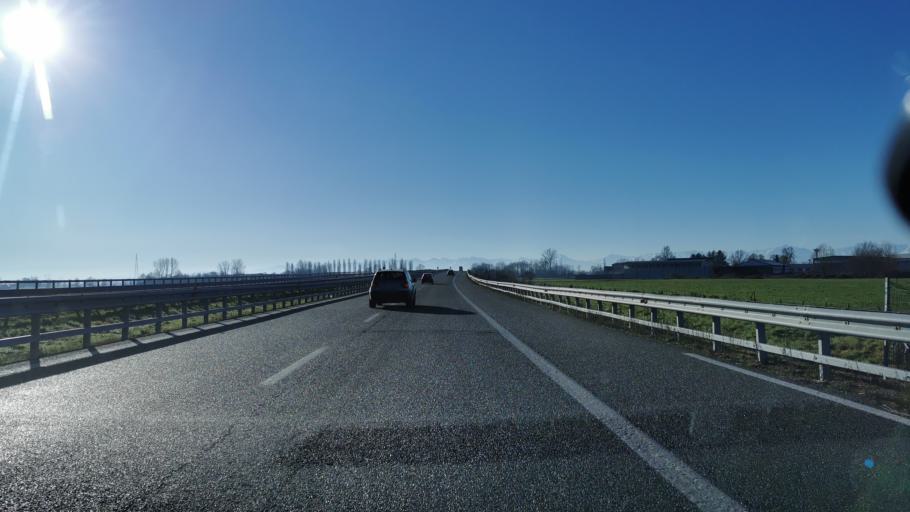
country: IT
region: Piedmont
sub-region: Provincia di Cuneo
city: Caramagna Piemonte
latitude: 44.7874
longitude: 7.7527
